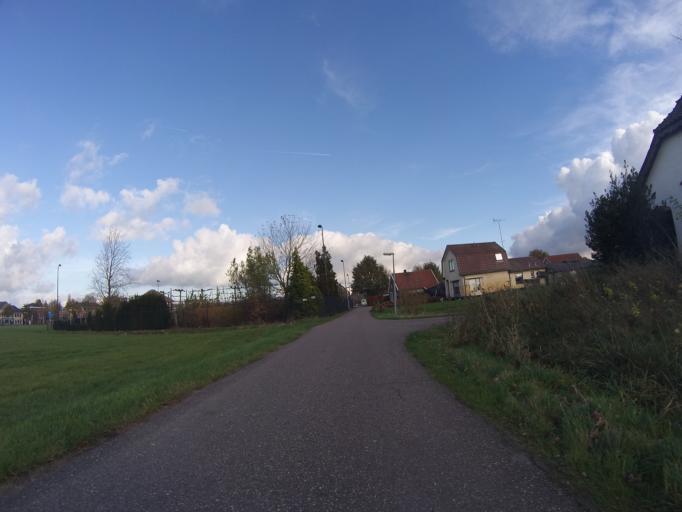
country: NL
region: Gelderland
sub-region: Gemeente Nijkerk
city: Nijkerk
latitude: 52.2134
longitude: 5.4750
